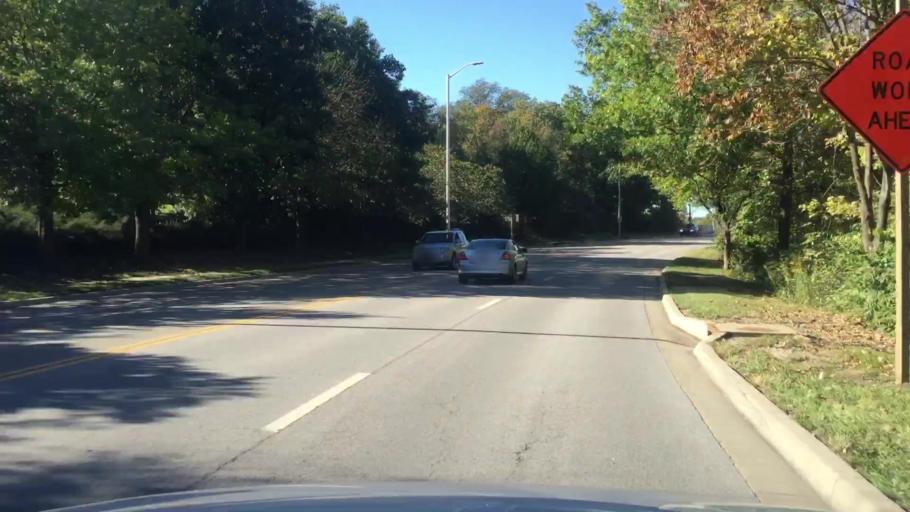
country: US
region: Kansas
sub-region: Johnson County
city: Leawood
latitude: 38.9296
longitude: -94.6283
